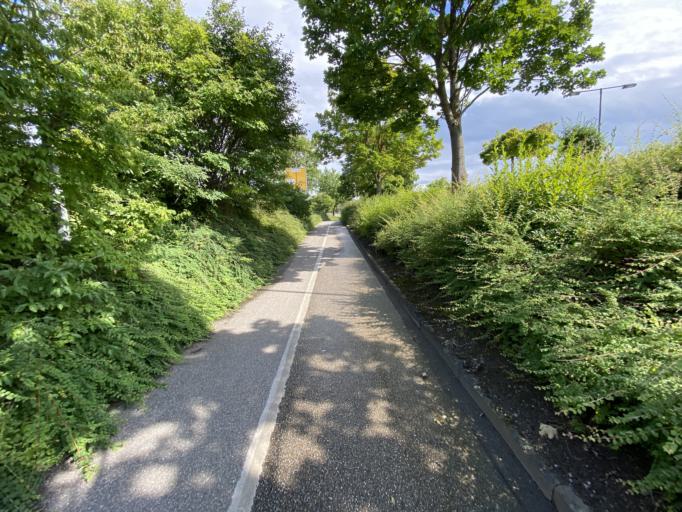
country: DE
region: Bavaria
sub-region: Lower Bavaria
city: Dingolfing
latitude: 48.6467
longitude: 12.4881
